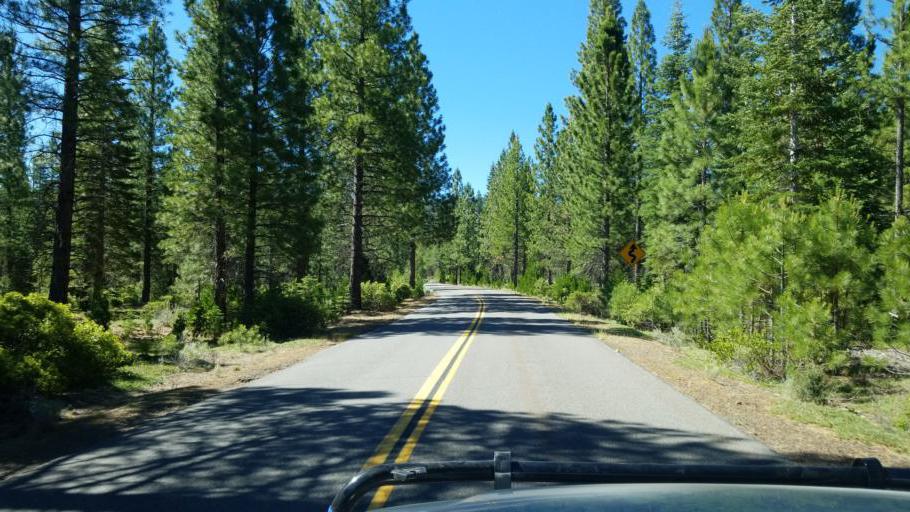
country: US
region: California
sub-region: Lassen County
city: Susanville
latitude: 40.5268
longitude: -120.7767
